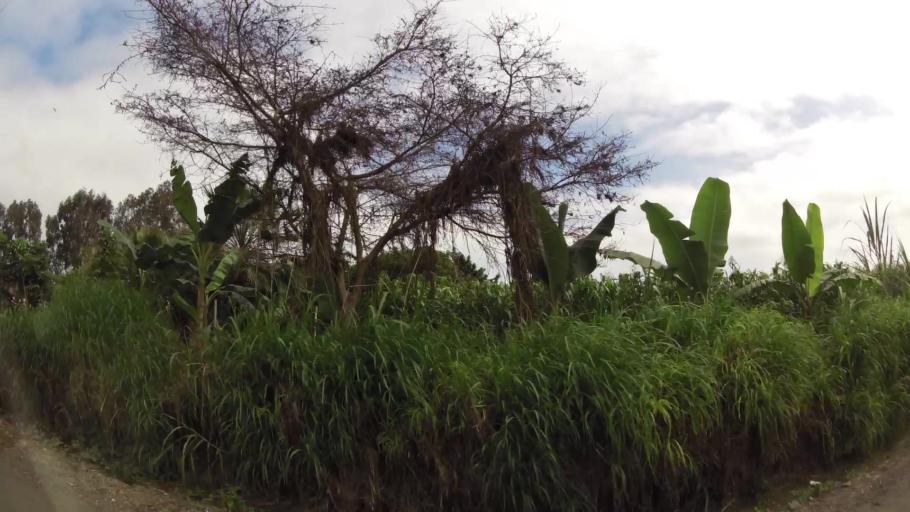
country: PE
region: Lima
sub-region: Provincia de Canete
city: Mala
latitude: -12.7267
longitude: -76.6184
